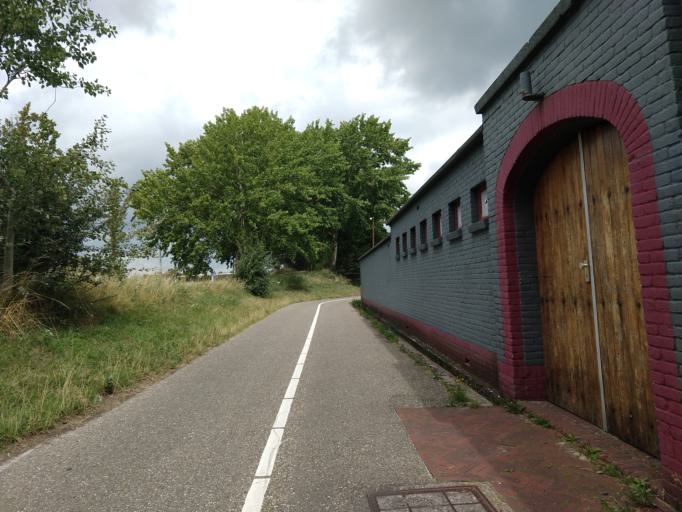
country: NL
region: Zeeland
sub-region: Gemeente Vlissingen
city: Vlissingen
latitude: 51.4526
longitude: 3.5871
